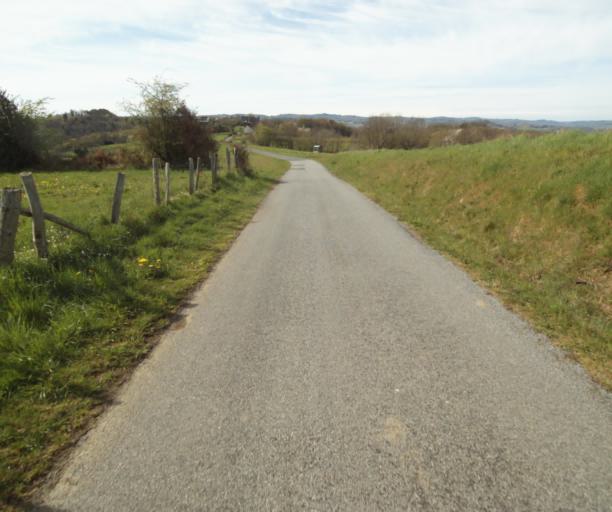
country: FR
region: Limousin
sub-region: Departement de la Correze
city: Laguenne
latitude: 45.2665
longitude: 1.8078
